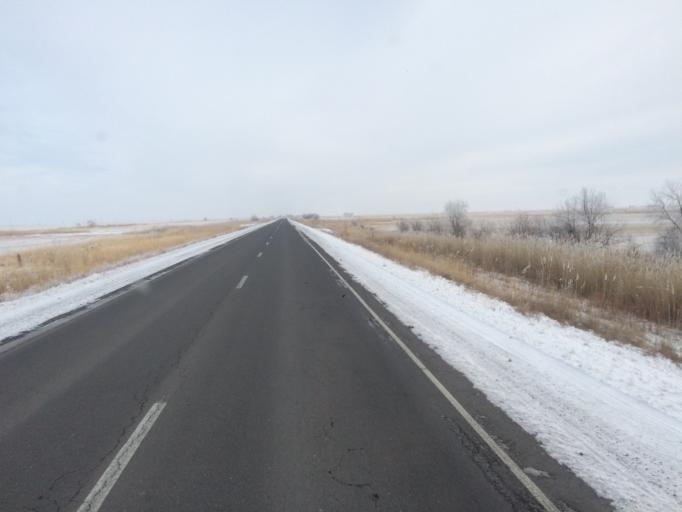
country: KG
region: Chuy
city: Tokmok
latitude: 43.3548
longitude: 75.4359
